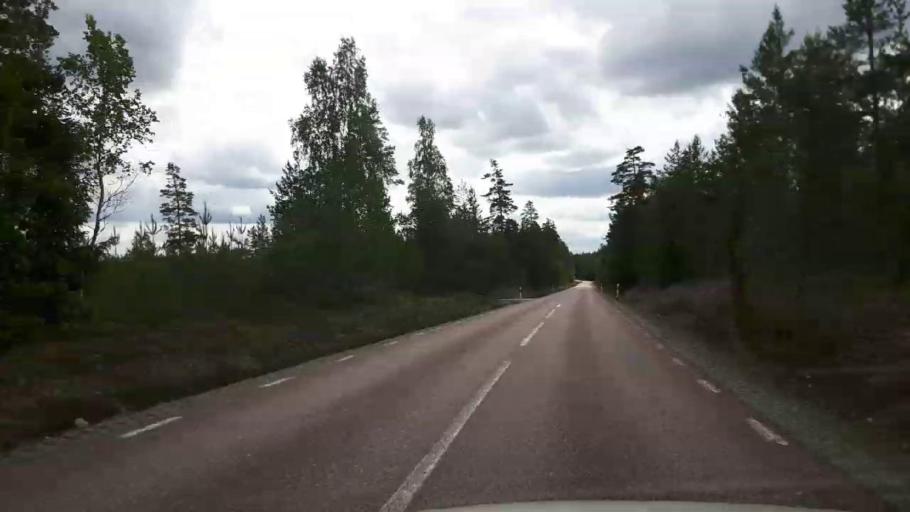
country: SE
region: Vaestmanland
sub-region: Fagersta Kommun
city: Fagersta
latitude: 59.8678
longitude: 15.8421
